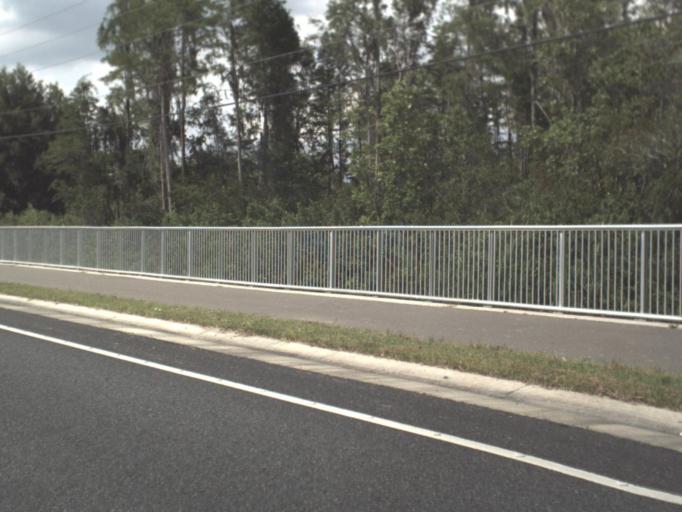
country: US
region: Florida
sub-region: Pasco County
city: Land O' Lakes
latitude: 28.2690
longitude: -82.4795
